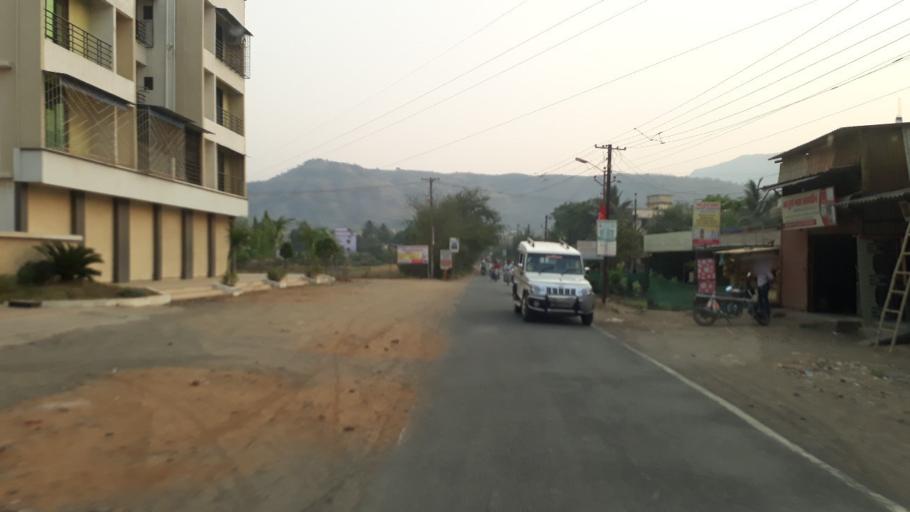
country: IN
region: Maharashtra
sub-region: Raigarh
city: Neral
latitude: 19.0256
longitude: 73.3220
